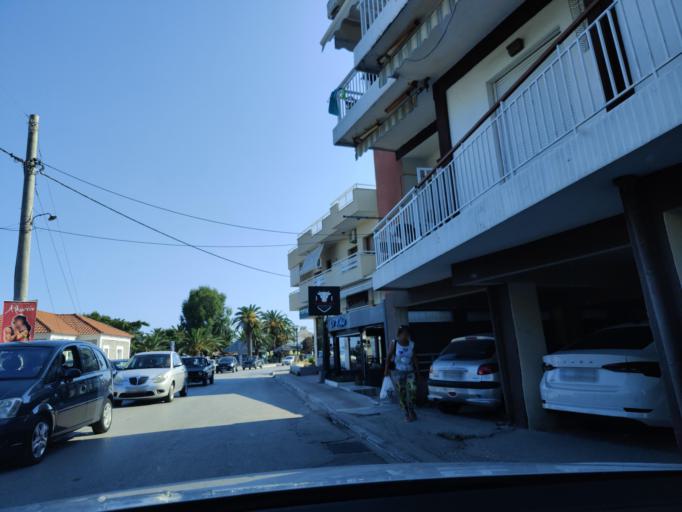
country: GR
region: East Macedonia and Thrace
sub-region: Nomos Kavalas
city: Nea Peramos
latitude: 40.8421
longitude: 24.3054
